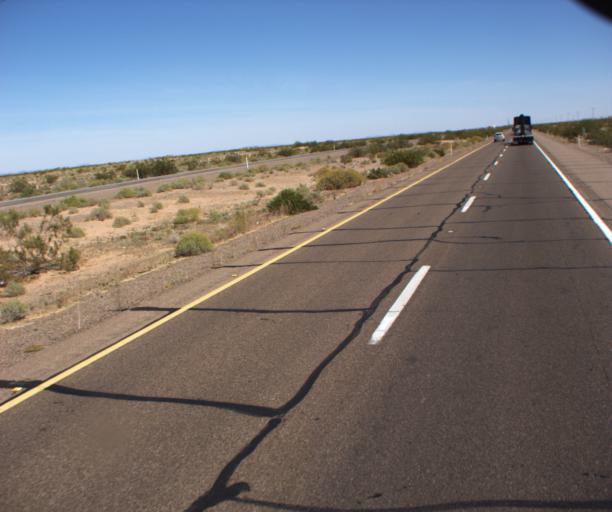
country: US
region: Arizona
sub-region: Yuma County
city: Wellton
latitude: 32.7766
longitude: -113.5935
